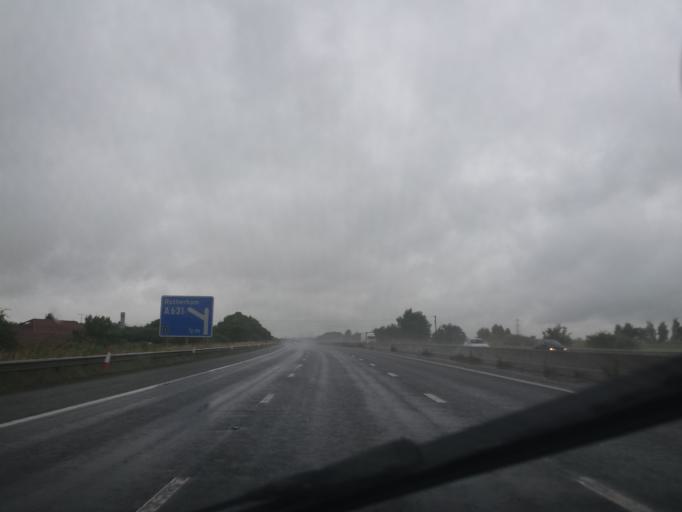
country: GB
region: England
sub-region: Rotherham
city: Hellaby
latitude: 53.4354
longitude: -1.2428
